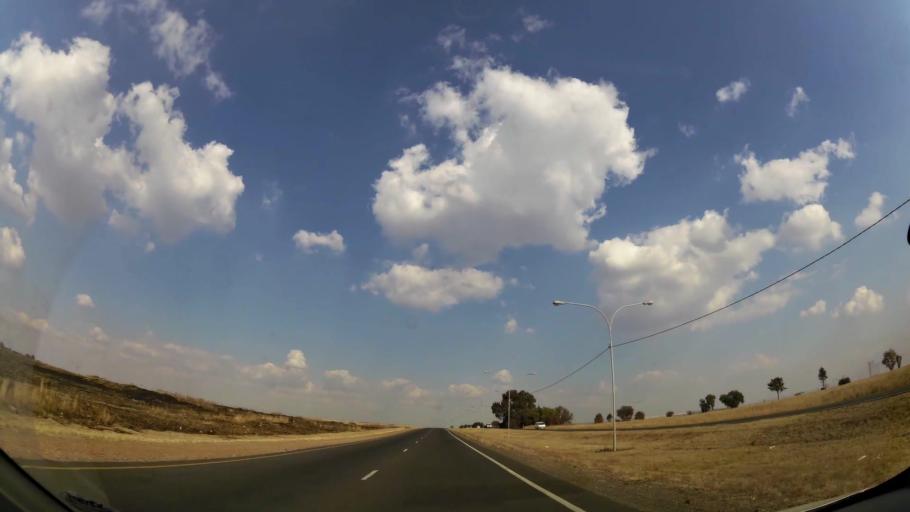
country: ZA
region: Gauteng
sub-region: Ekurhuleni Metropolitan Municipality
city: Brakpan
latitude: -26.2779
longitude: 28.3291
